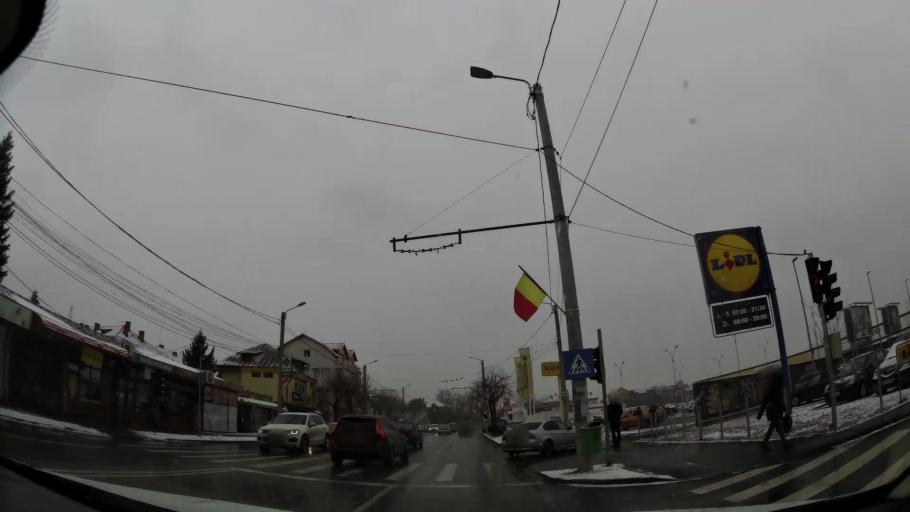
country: RO
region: Dambovita
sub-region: Municipiul Targoviste
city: Targoviste
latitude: 44.9190
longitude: 25.4607
